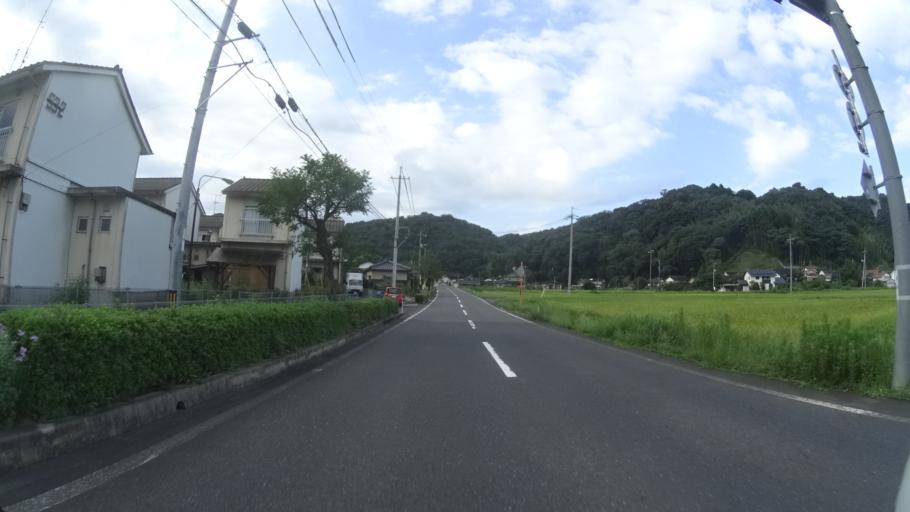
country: JP
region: Tottori
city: Kurayoshi
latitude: 35.4767
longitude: 133.9059
